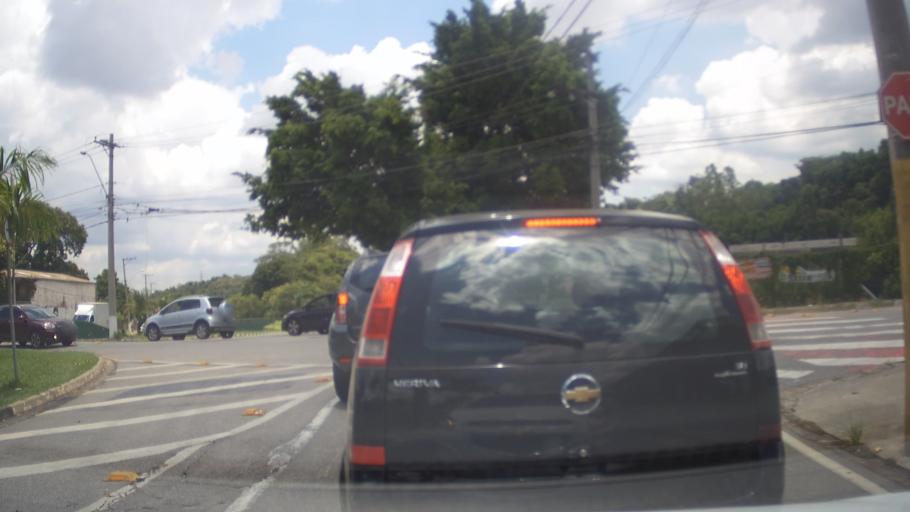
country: BR
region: Sao Paulo
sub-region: Vinhedo
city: Vinhedo
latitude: -23.0121
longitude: -46.9812
